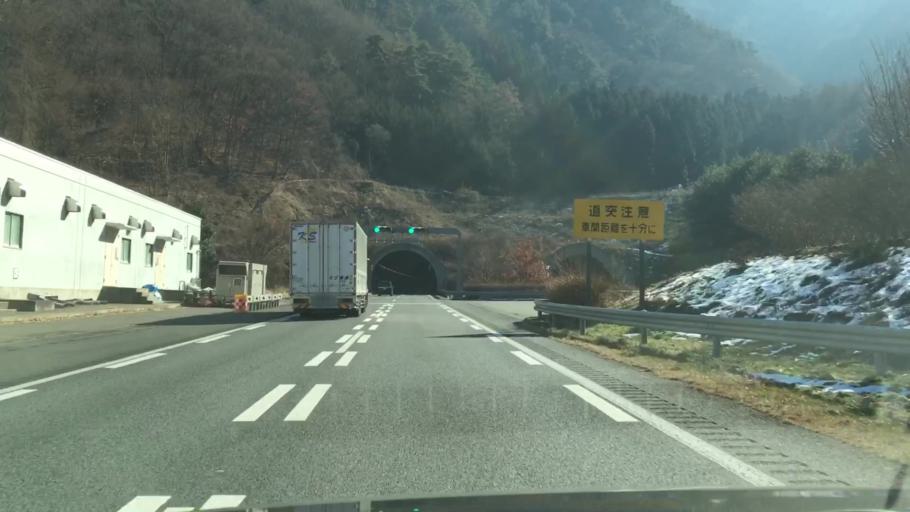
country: JP
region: Nagano
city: Nagano-shi
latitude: 36.5099
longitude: 138.1577
